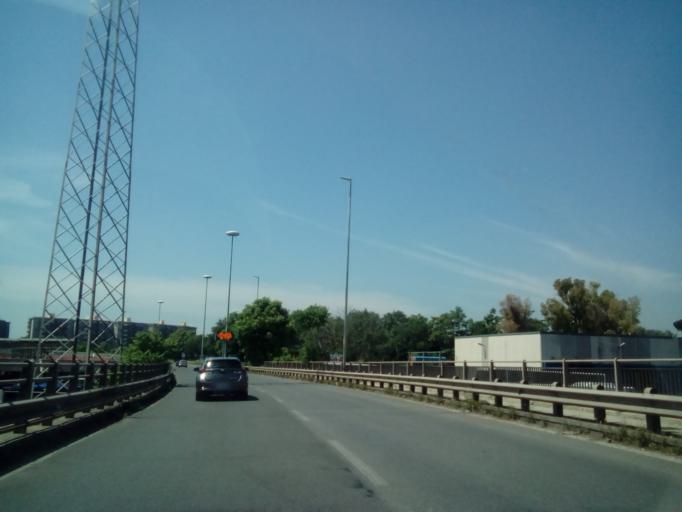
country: IT
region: Latium
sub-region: Citta metropolitana di Roma Capitale
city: Rome
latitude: 41.9229
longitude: 12.5660
